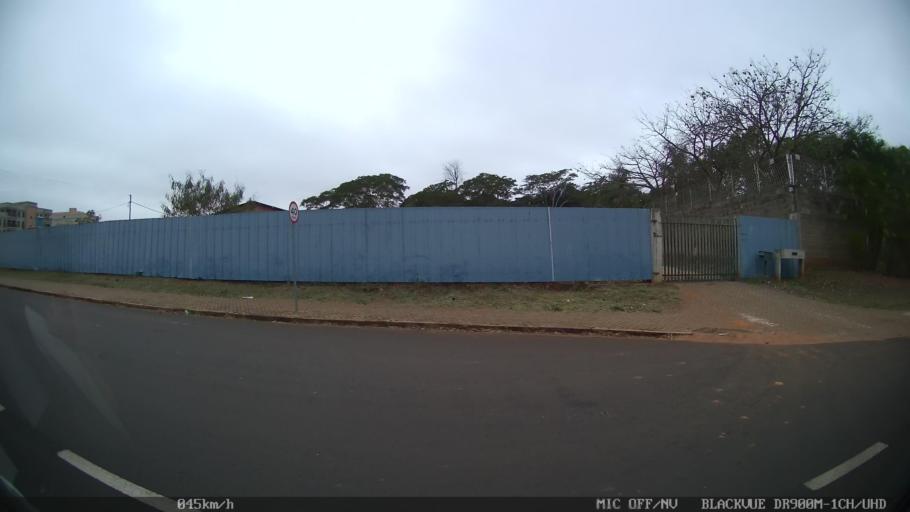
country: BR
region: Sao Paulo
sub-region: Sao Jose Do Rio Preto
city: Sao Jose do Rio Preto
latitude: -20.8488
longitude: -49.4035
